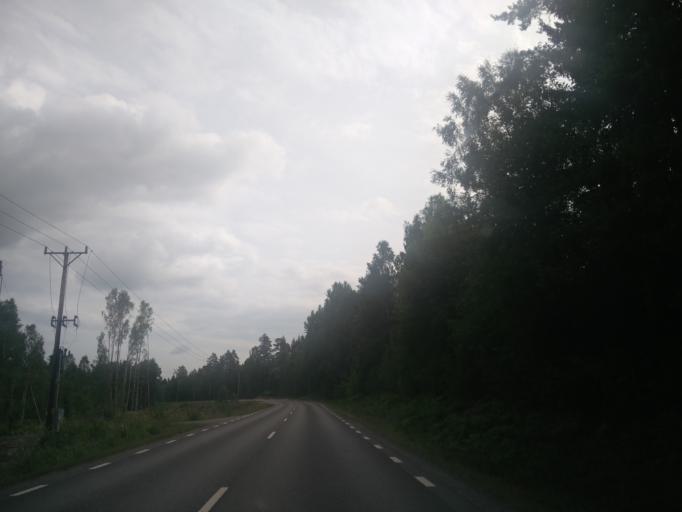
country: SE
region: Vaermland
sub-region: Arvika Kommun
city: Arvika
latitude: 59.7189
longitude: 12.5678
